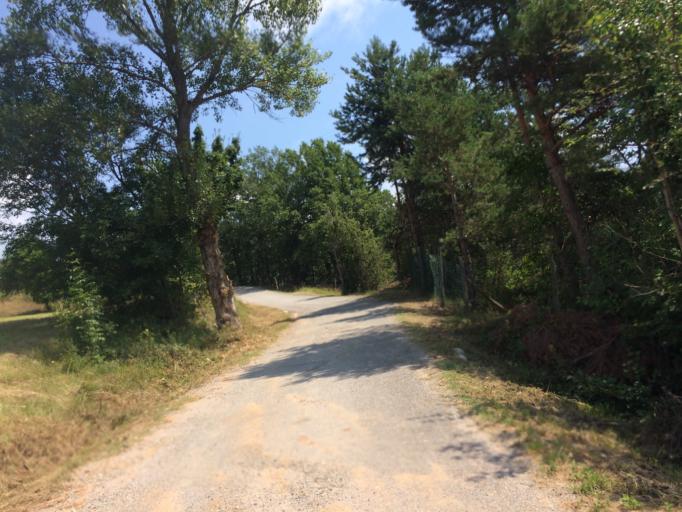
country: IT
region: Liguria
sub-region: Provincia di Savona
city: Massimino
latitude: 44.3159
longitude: 8.0613
